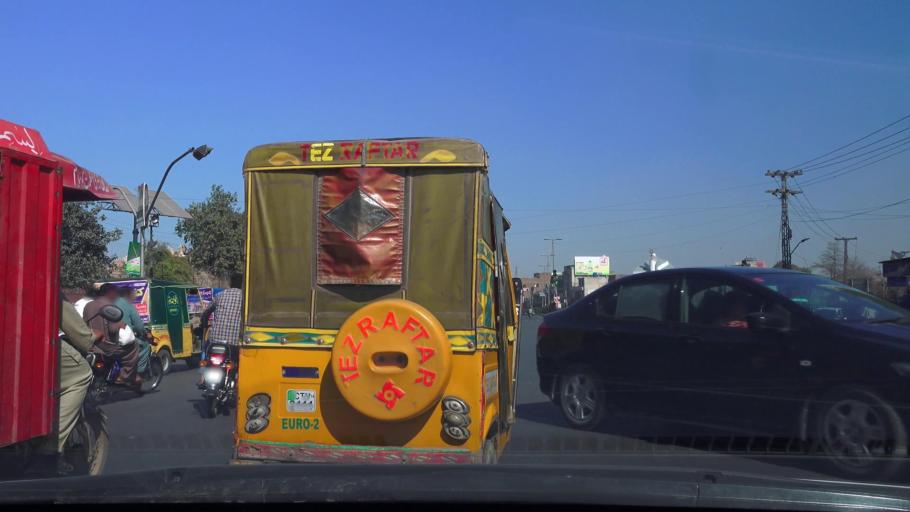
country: PK
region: Punjab
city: Faisalabad
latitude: 31.4116
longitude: 73.0614
